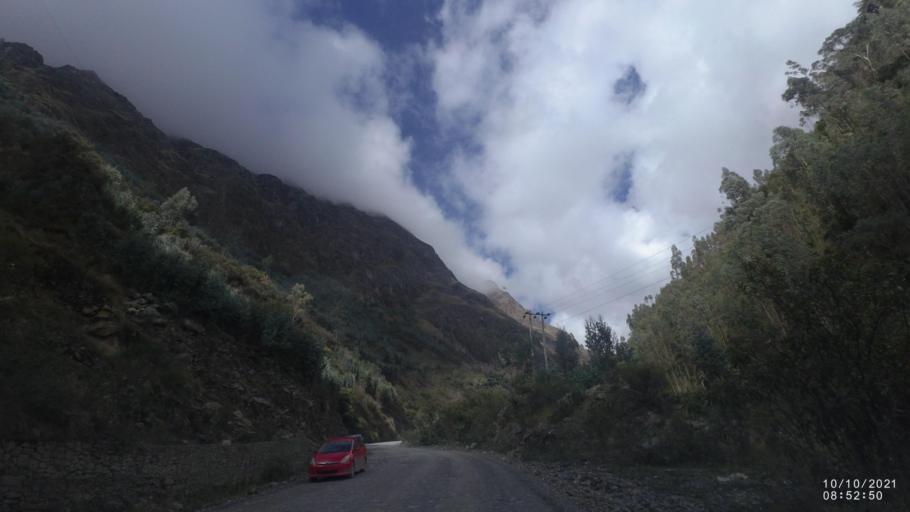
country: BO
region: La Paz
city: Quime
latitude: -16.9865
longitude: -67.2301
